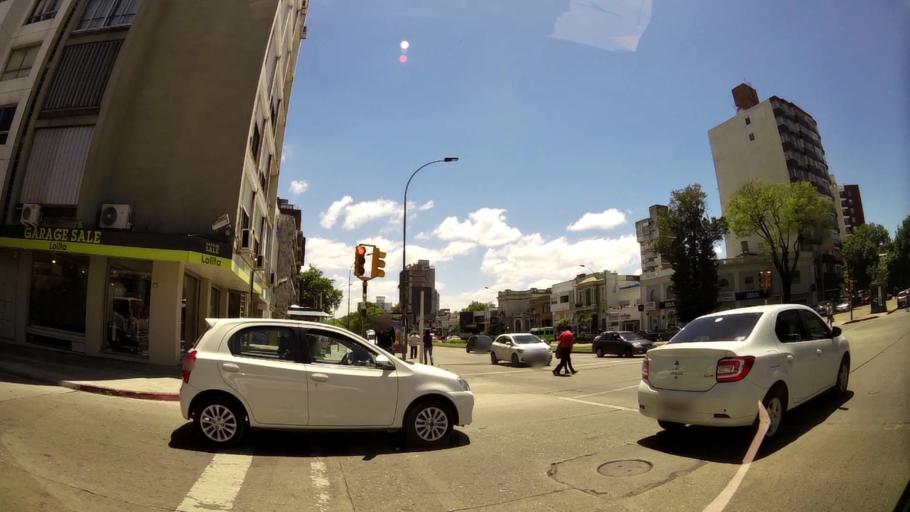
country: UY
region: Montevideo
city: Montevideo
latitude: -34.8917
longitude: -56.1656
